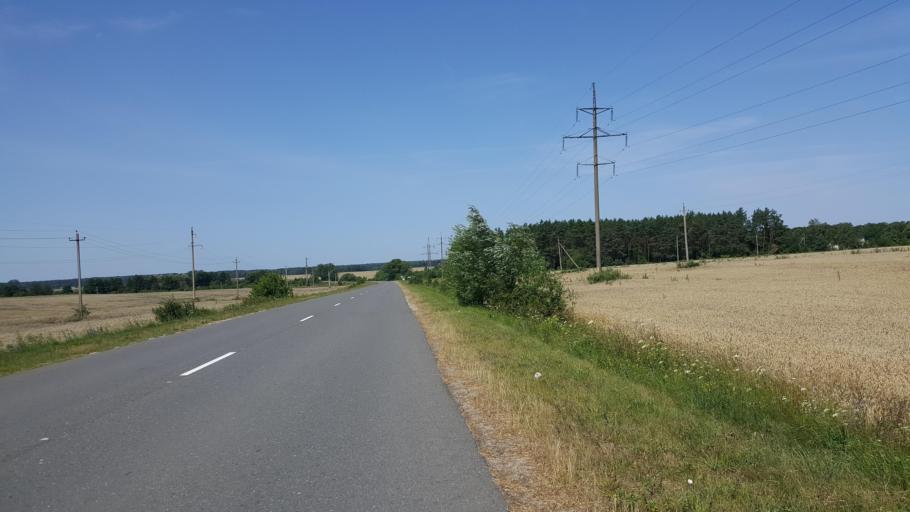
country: BY
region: Brest
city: Kamyanyets
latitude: 52.3801
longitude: 23.6616
